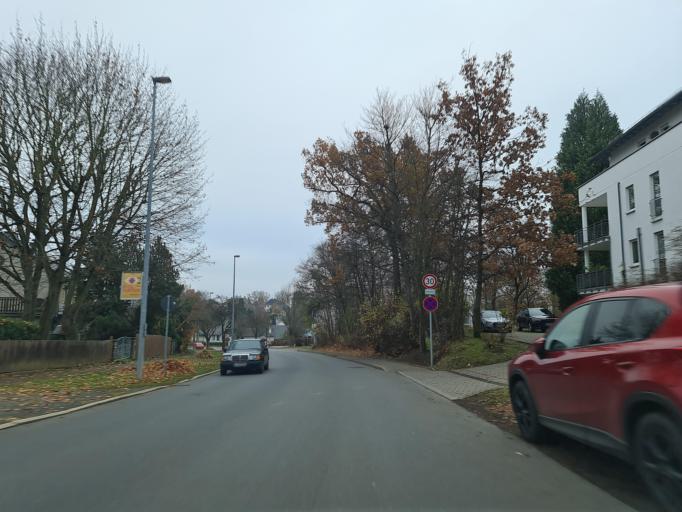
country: DE
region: Saxony
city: Plauen
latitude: 50.4986
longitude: 12.1048
